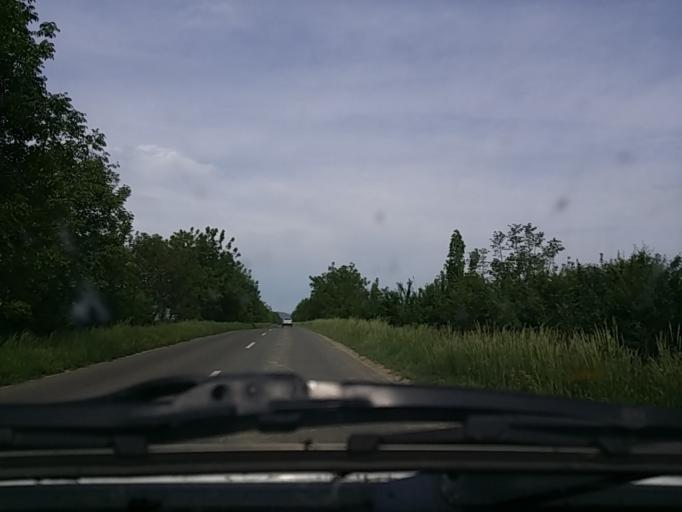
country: HR
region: Osjecko-Baranjska
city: Viljevo
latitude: 45.8283
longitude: 18.1097
